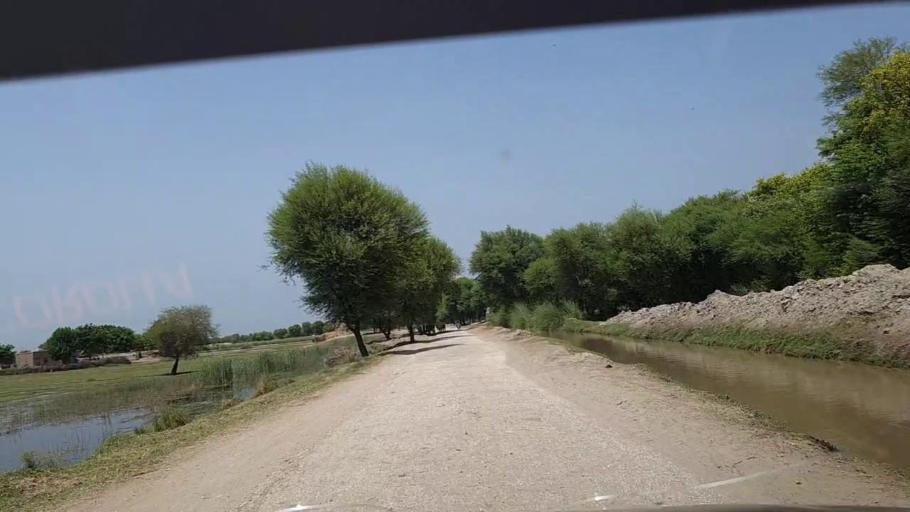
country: PK
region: Sindh
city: Khanpur
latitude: 27.8119
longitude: 69.4504
